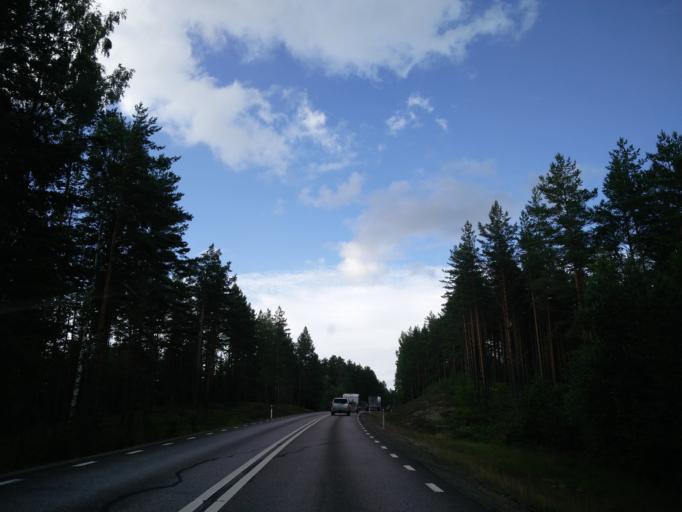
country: SE
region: Vaermland
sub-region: Hagfors Kommun
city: Ekshaerad
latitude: 60.4297
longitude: 13.2558
